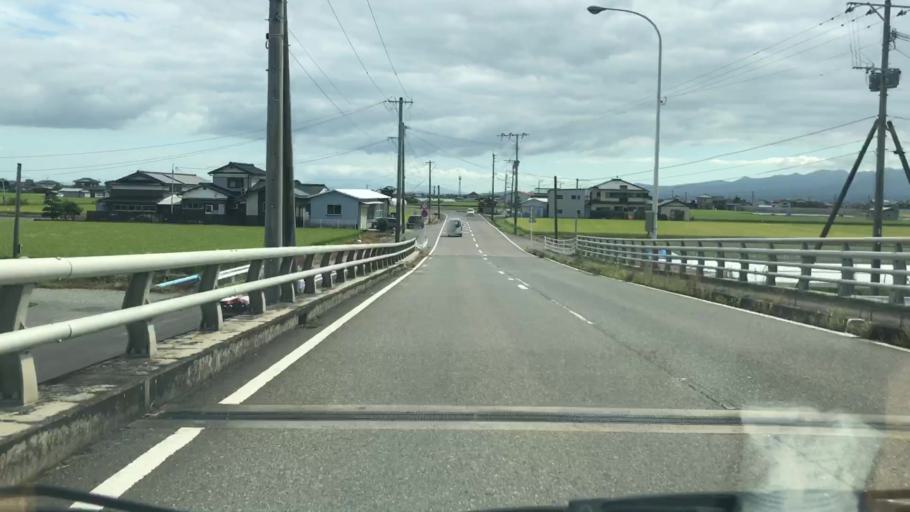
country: JP
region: Saga Prefecture
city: Saga-shi
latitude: 33.1985
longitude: 130.1813
